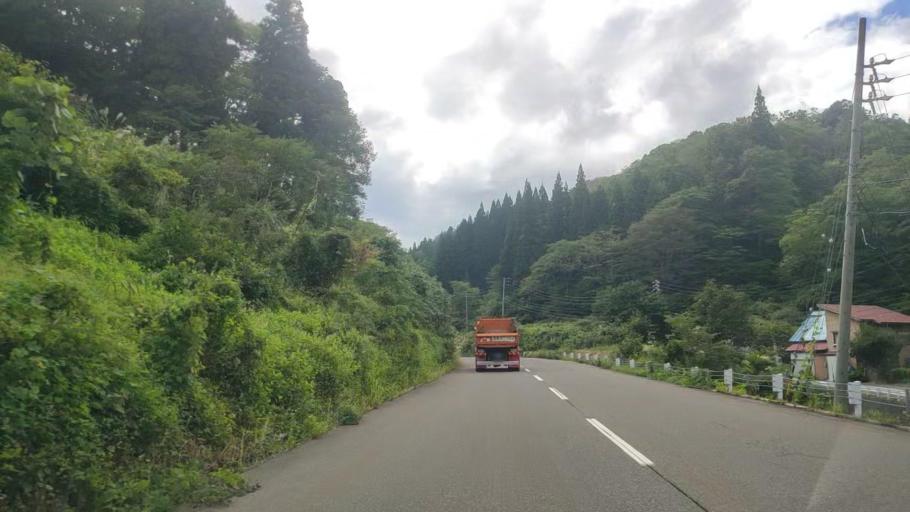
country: JP
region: Nagano
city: Iiyama
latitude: 36.8952
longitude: 138.3214
